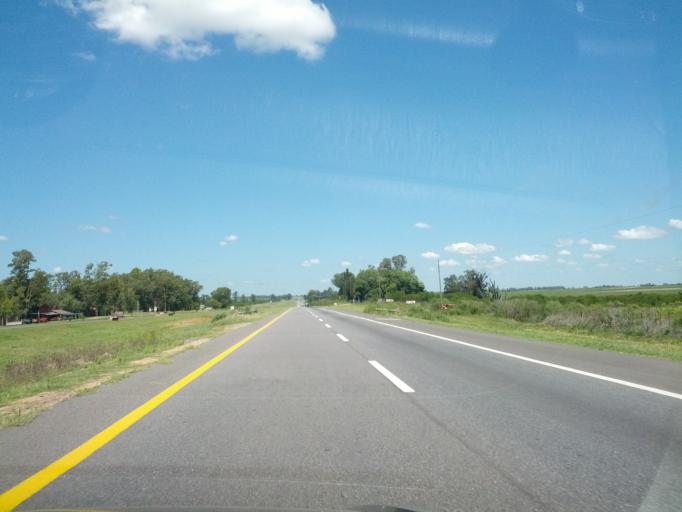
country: AR
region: Entre Rios
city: Gualeguaychu
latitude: -33.1208
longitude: -58.6525
